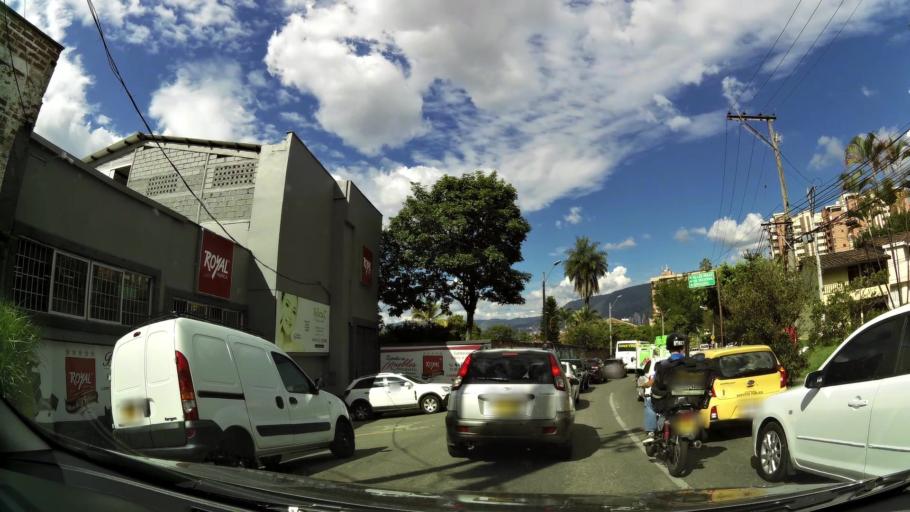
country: CO
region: Antioquia
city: Sabaneta
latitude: 6.1596
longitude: -75.6033
